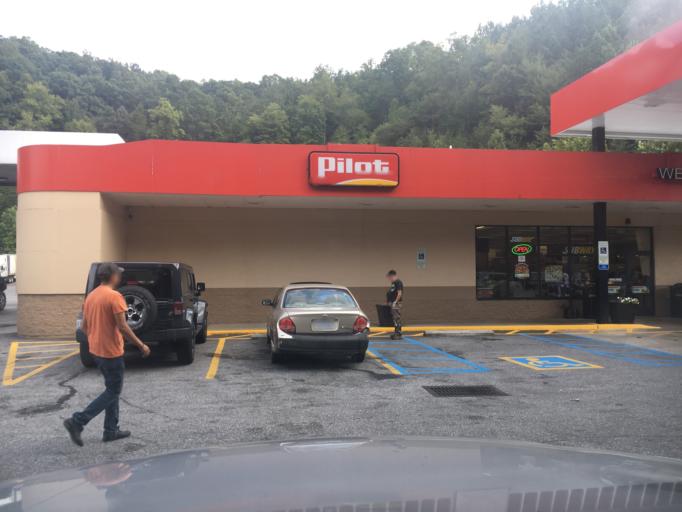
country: US
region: North Carolina
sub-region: McDowell County
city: West Marion
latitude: 35.6427
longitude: -82.0402
